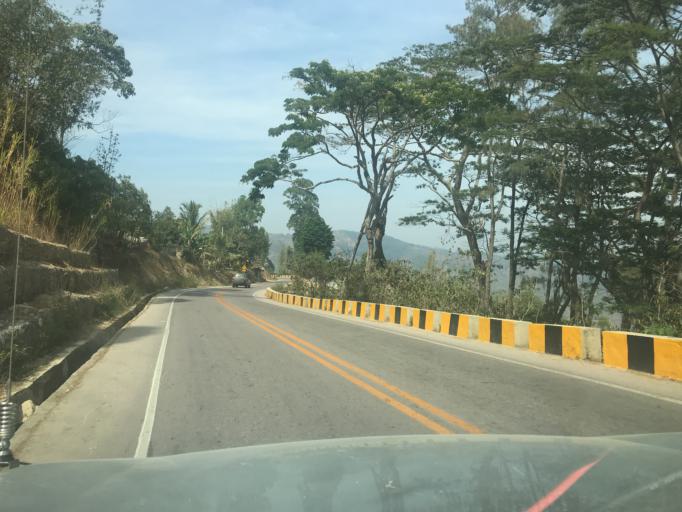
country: TL
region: Aileu
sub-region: Aileu Villa
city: Aileu
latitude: -8.6736
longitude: 125.5520
